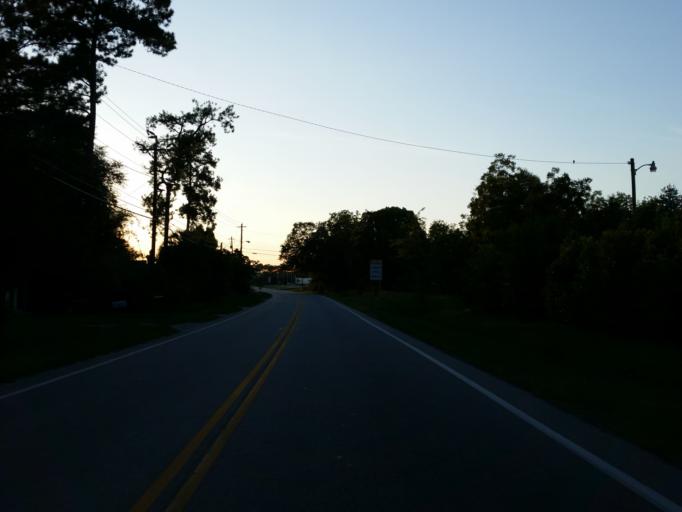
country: US
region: Georgia
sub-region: Berrien County
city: Nashville
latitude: 31.2109
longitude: -83.2553
